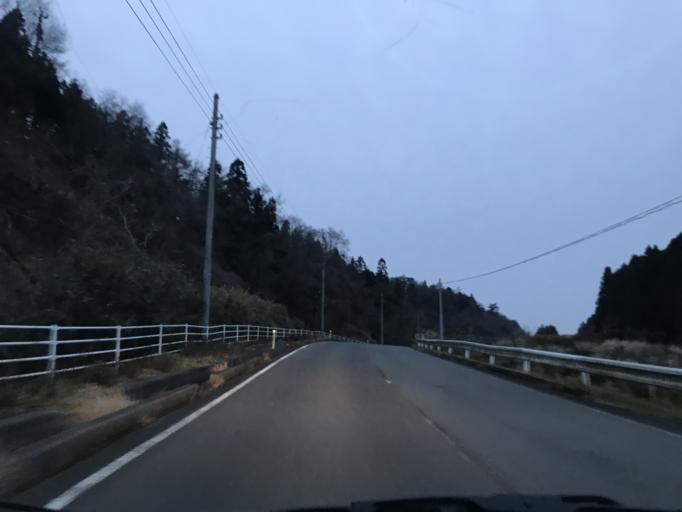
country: JP
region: Iwate
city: Ichinoseki
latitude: 38.8178
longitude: 141.1165
